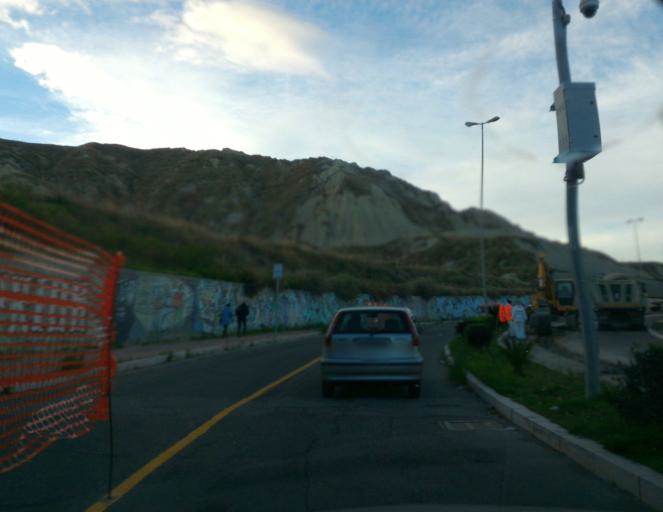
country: IT
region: Calabria
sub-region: Provincia di Crotone
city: Crotone
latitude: 39.0672
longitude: 17.1295
